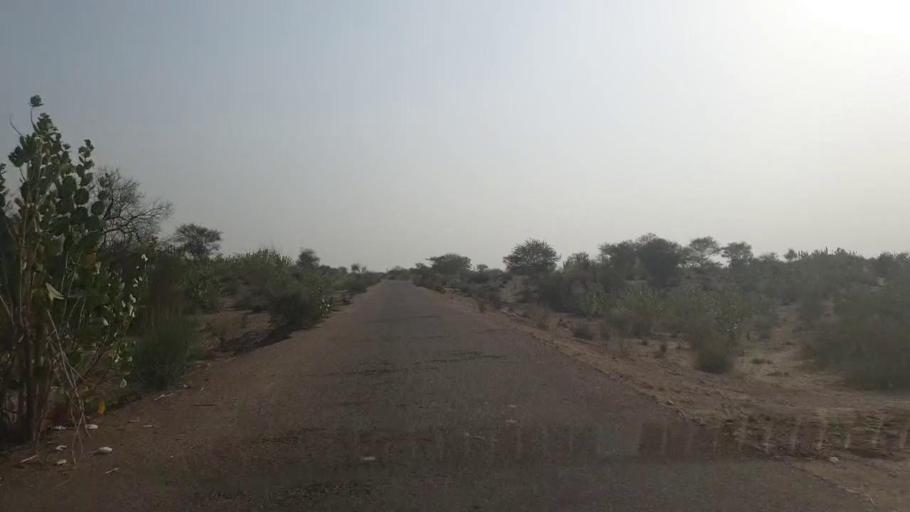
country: PK
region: Sindh
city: Chor
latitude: 25.4689
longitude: 69.9687
